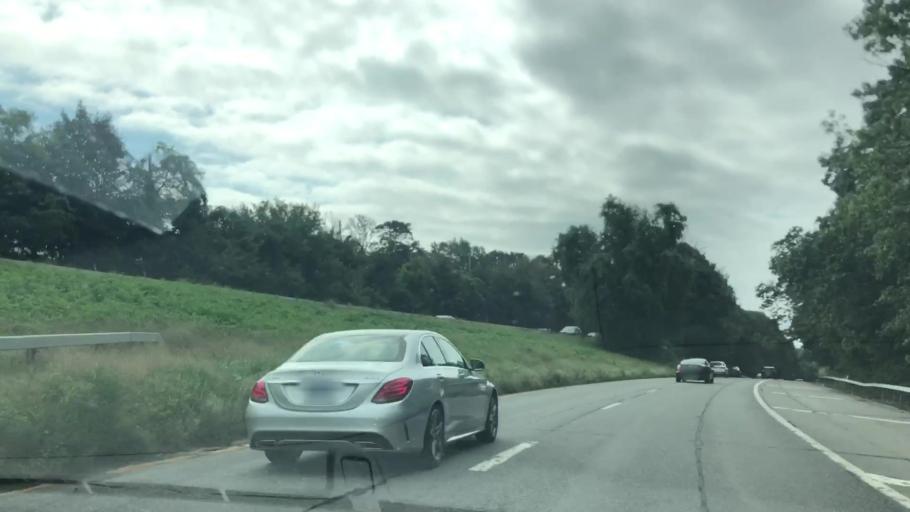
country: US
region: New York
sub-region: Westchester County
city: Yonkers
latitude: 40.9466
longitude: -73.8725
